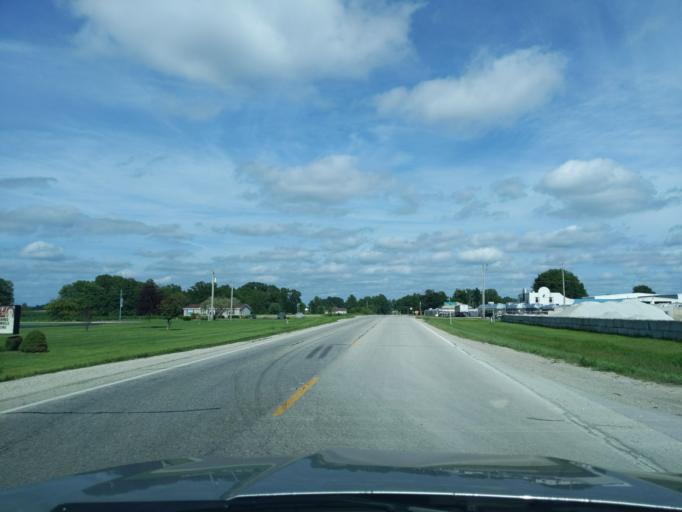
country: US
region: Indiana
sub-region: Ripley County
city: Batesville
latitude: 39.3112
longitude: -85.3365
